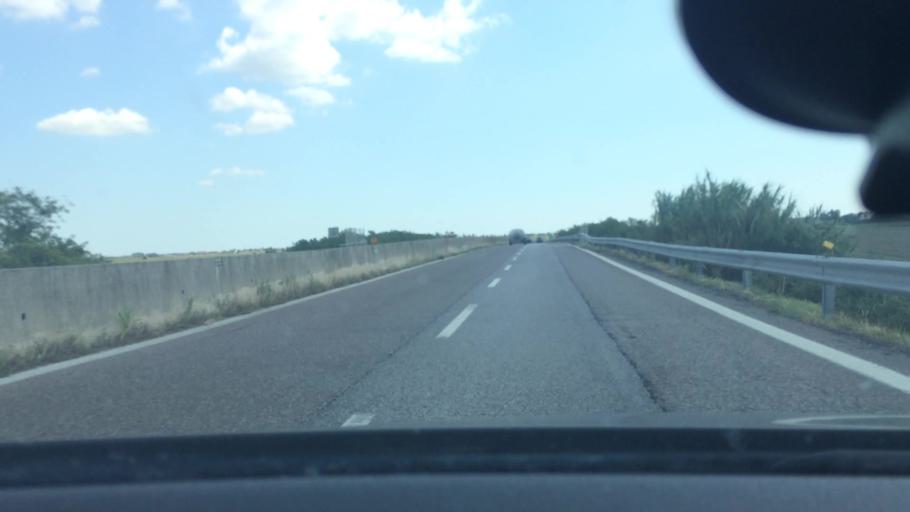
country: IT
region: Emilia-Romagna
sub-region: Provincia di Ferrara
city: Ostellato
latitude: 44.7561
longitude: 11.9627
